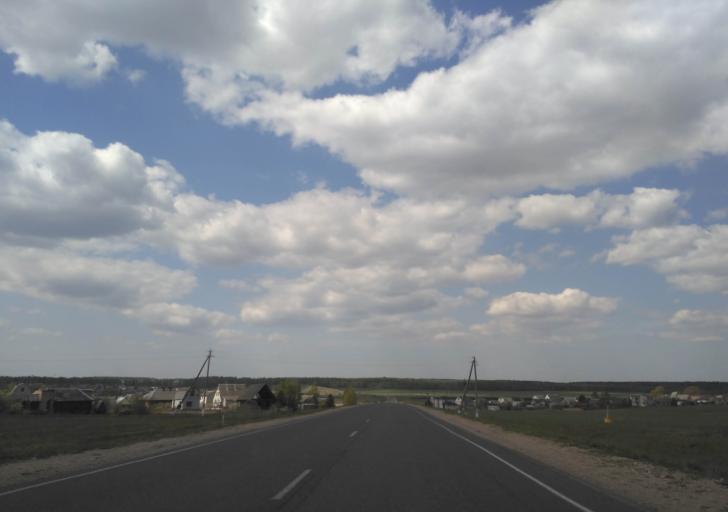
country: BY
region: Minsk
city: Vilyeyka
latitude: 54.5165
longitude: 26.9825
